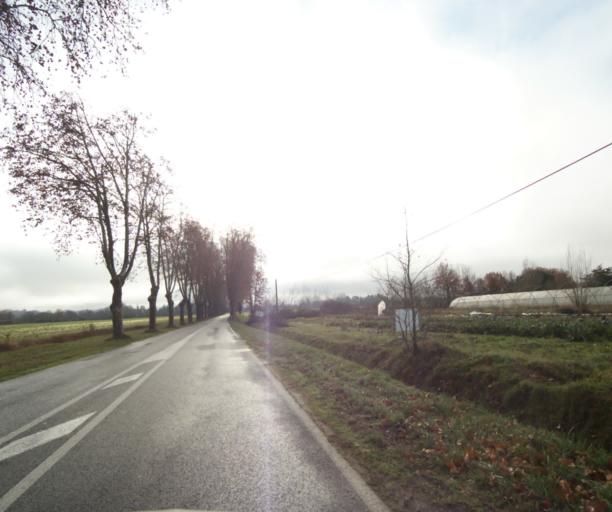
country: FR
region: Midi-Pyrenees
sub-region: Departement de la Haute-Garonne
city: Villemur-sur-Tarn
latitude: 43.8830
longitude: 1.4818
